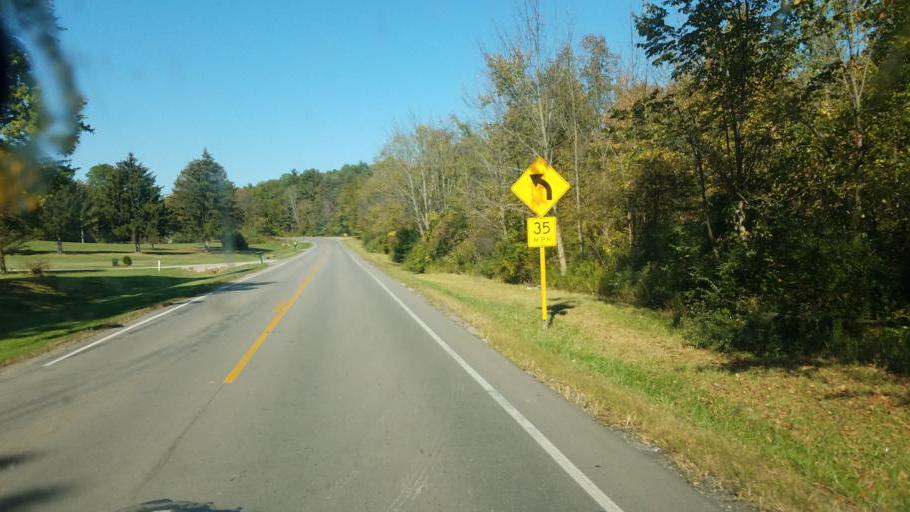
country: US
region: Ohio
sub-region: Richland County
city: Lexington
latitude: 40.7060
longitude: -82.6427
